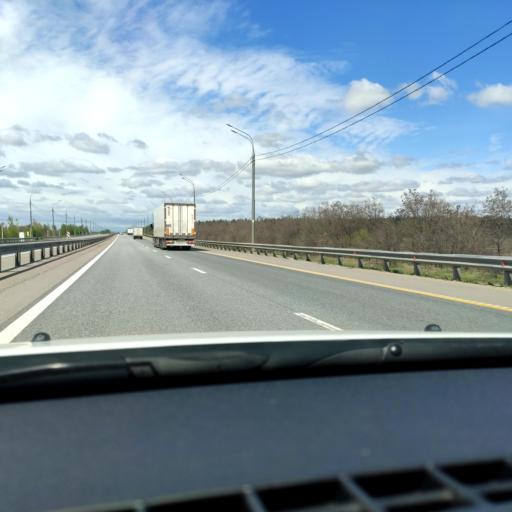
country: RU
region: Lipetsk
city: Khlevnoye
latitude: 52.1621
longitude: 39.1968
